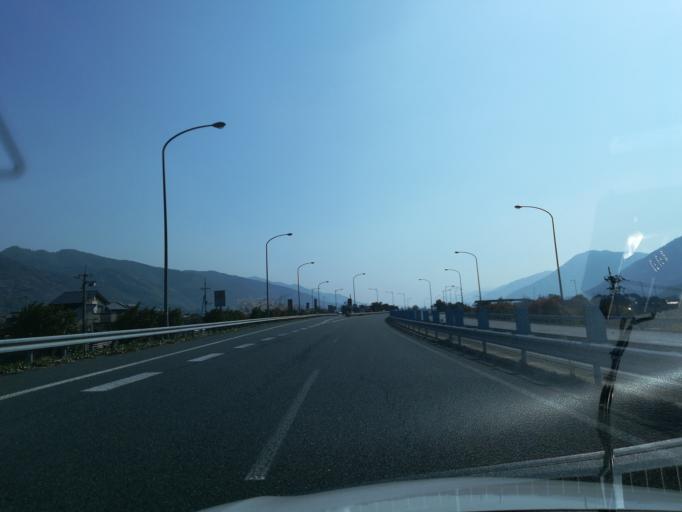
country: JP
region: Tokushima
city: Ikedacho
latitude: 34.0376
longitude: 133.8910
